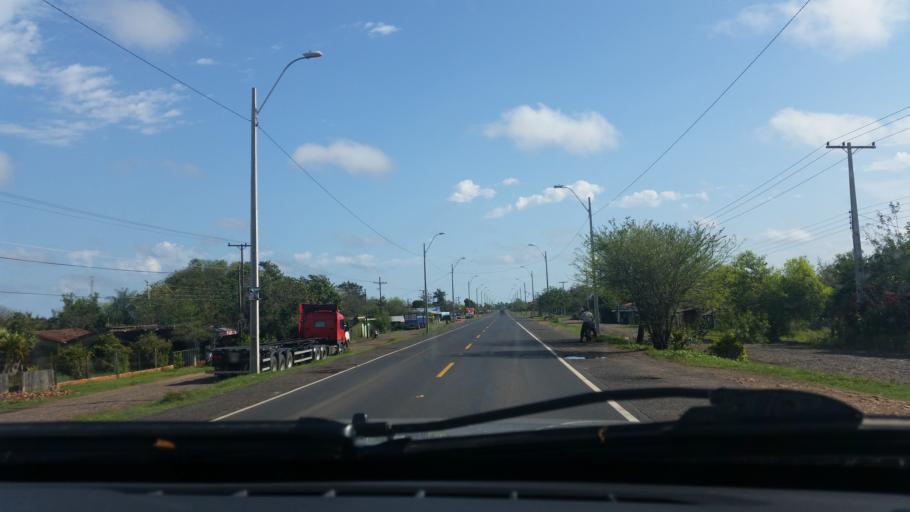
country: PY
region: Presidente Hayes
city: Benjamin Aceval
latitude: -24.9504
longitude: -57.5512
